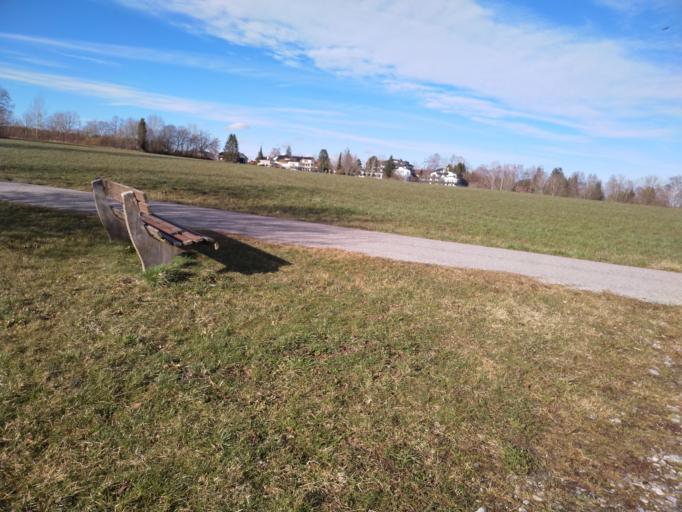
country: DE
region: Bavaria
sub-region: Swabia
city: Bad Worishofen
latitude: 47.9952
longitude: 10.5809
